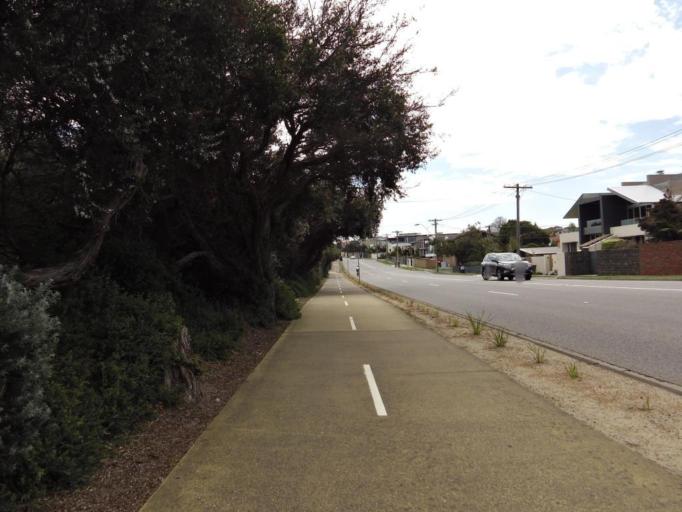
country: AU
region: Victoria
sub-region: Bayside
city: Black Rock
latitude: -37.9692
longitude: 145.0118
